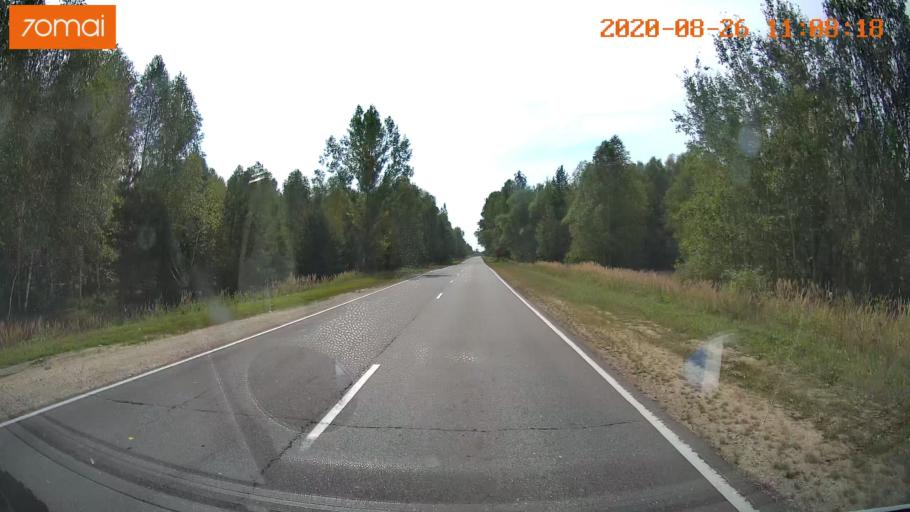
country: RU
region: Rjazan
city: Izhevskoye
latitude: 54.5064
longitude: 41.1218
